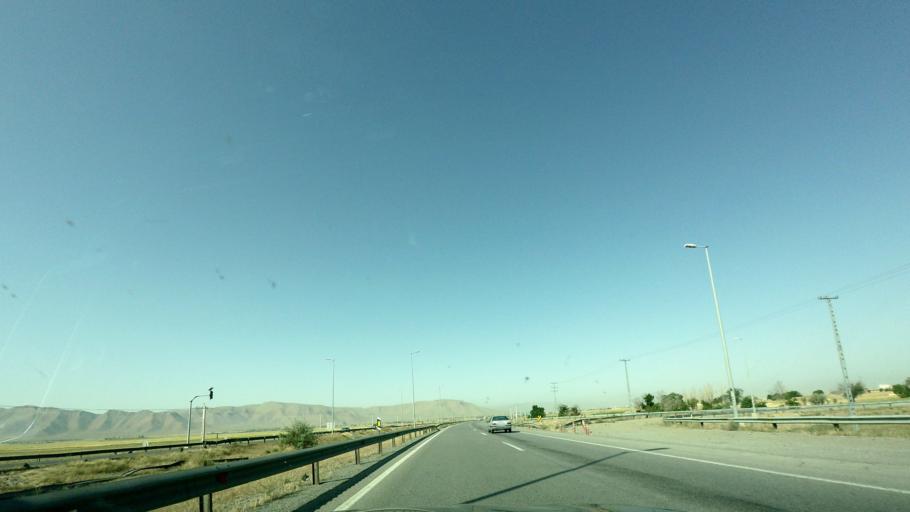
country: IR
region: Markazi
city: Arak
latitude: 34.1682
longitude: 50.0321
